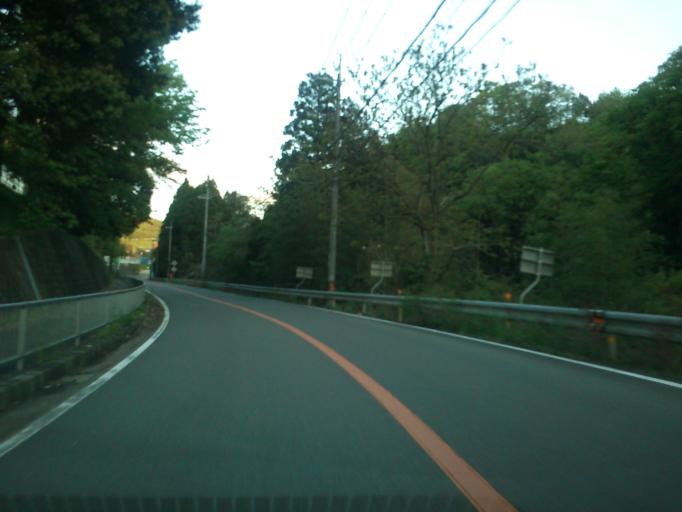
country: JP
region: Kyoto
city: Ayabe
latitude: 35.2160
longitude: 135.4202
